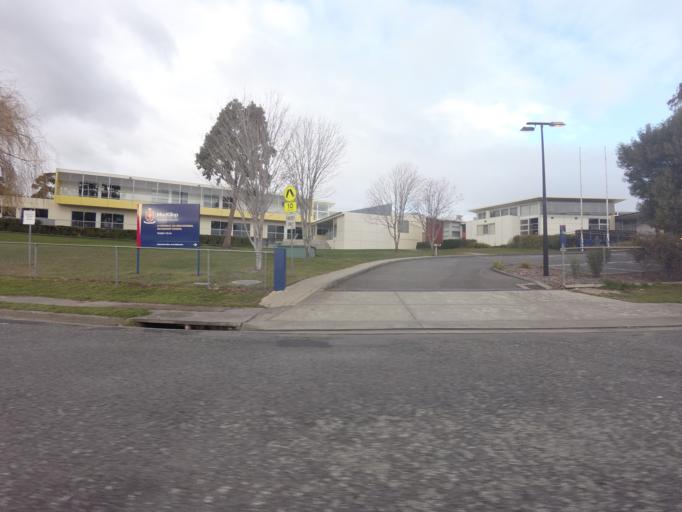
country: AU
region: Tasmania
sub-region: Clarence
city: Warrane
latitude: -42.8576
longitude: 147.3996
